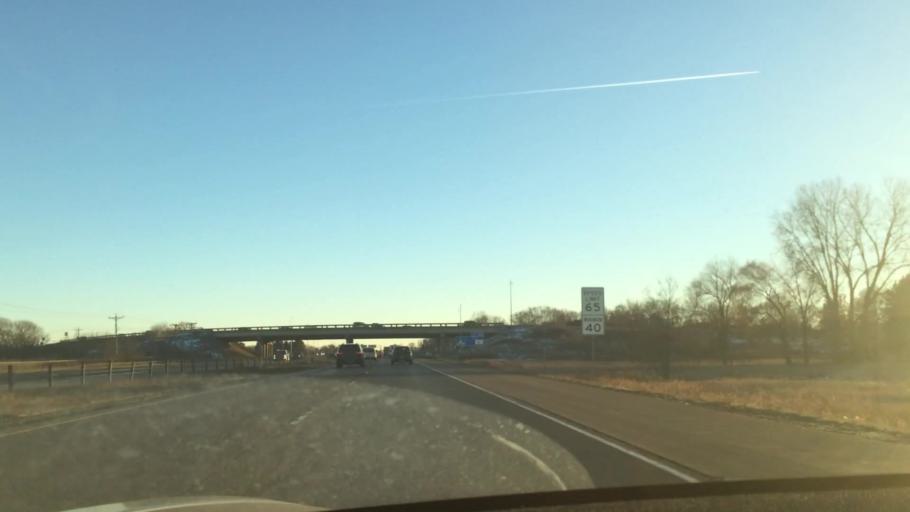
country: US
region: Minnesota
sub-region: Ramsey County
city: Mounds View
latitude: 45.1179
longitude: -93.1886
